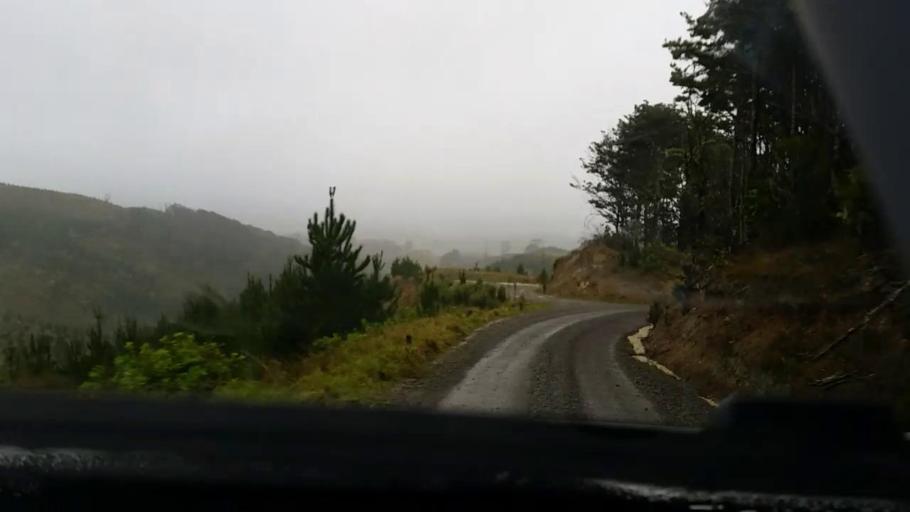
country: NZ
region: Wellington
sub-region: Masterton District
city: Masterton
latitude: -41.2026
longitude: 175.8122
